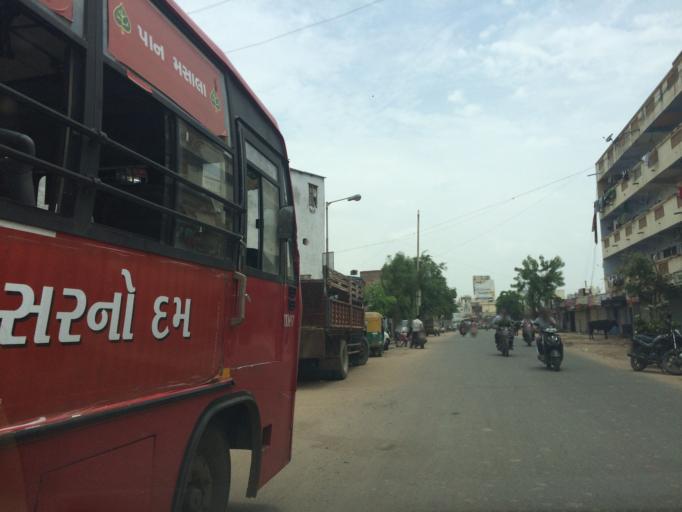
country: IN
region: Gujarat
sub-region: Ahmadabad
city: Ahmedabad
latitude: 23.0865
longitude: 72.5648
